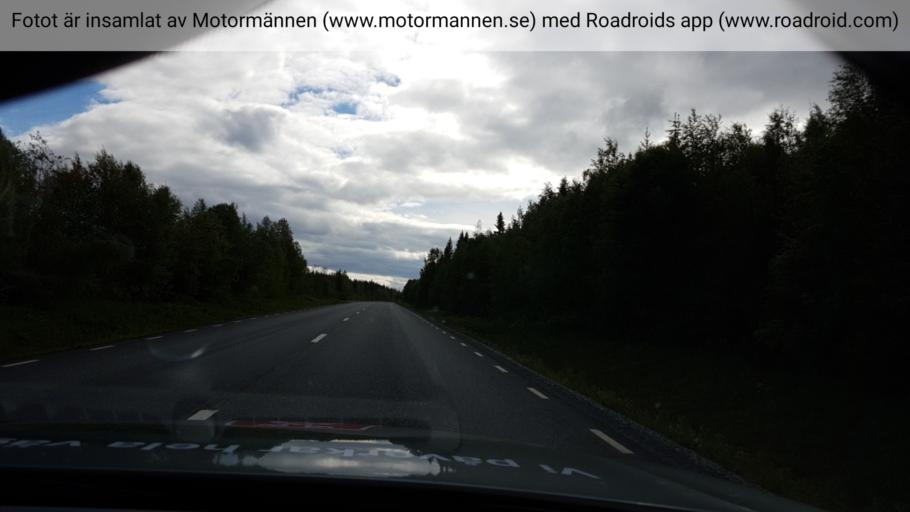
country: SE
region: Jaemtland
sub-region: Stroemsunds Kommun
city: Stroemsund
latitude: 64.1172
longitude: 15.6202
